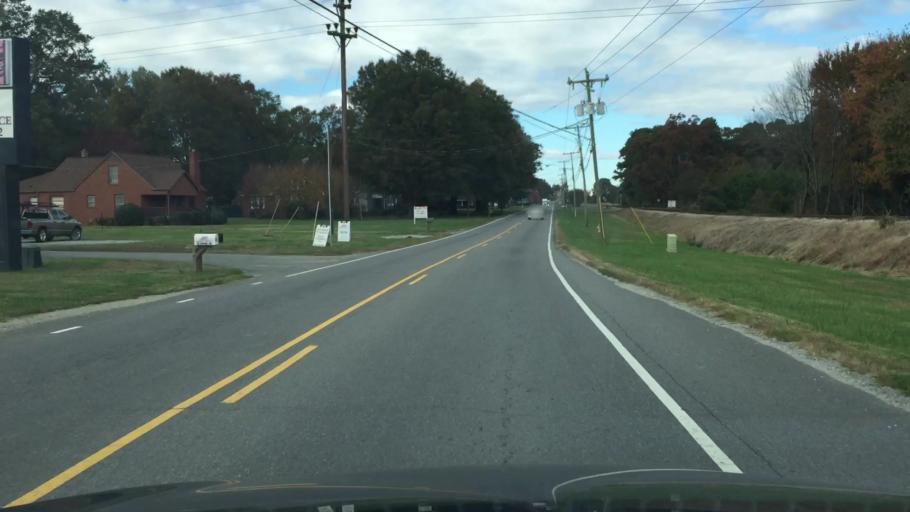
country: US
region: North Carolina
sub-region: Iredell County
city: Mooresville
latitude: 35.6037
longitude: -80.8142
